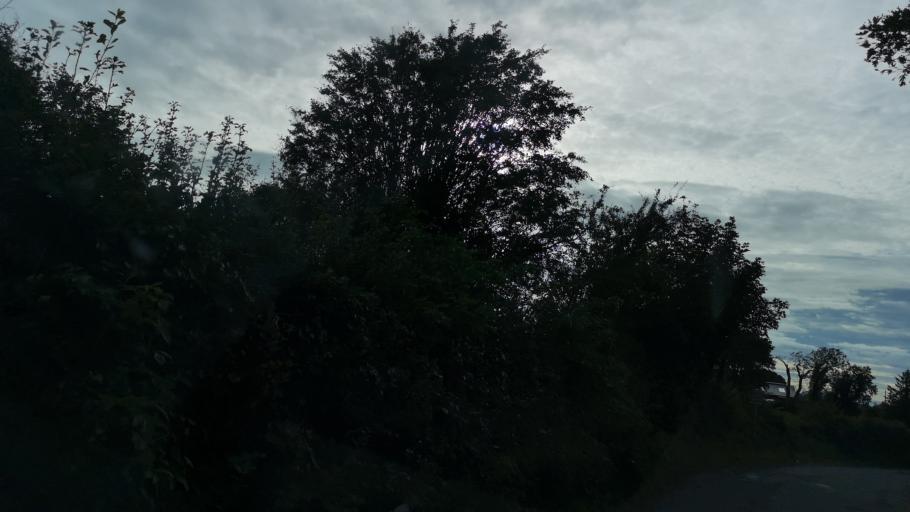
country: IE
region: Connaught
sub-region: County Galway
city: Ballinasloe
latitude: 53.3600
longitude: -8.2206
